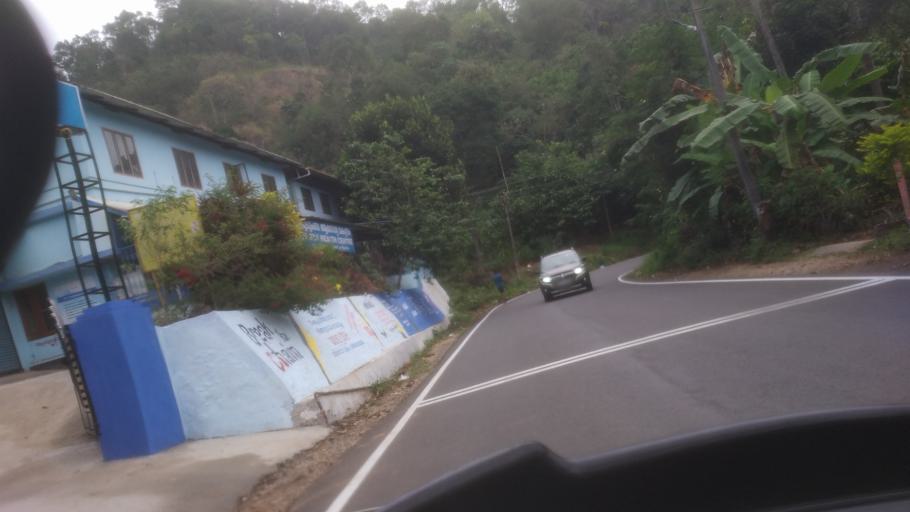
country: IN
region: Kerala
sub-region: Idukki
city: Idukki
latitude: 9.9442
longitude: 77.0208
